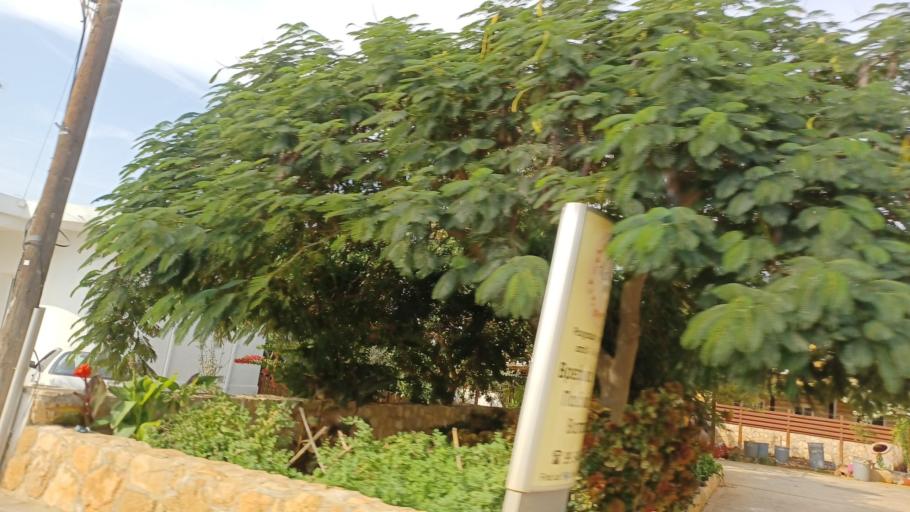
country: CY
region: Ammochostos
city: Frenaros
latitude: 35.0403
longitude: 33.9211
